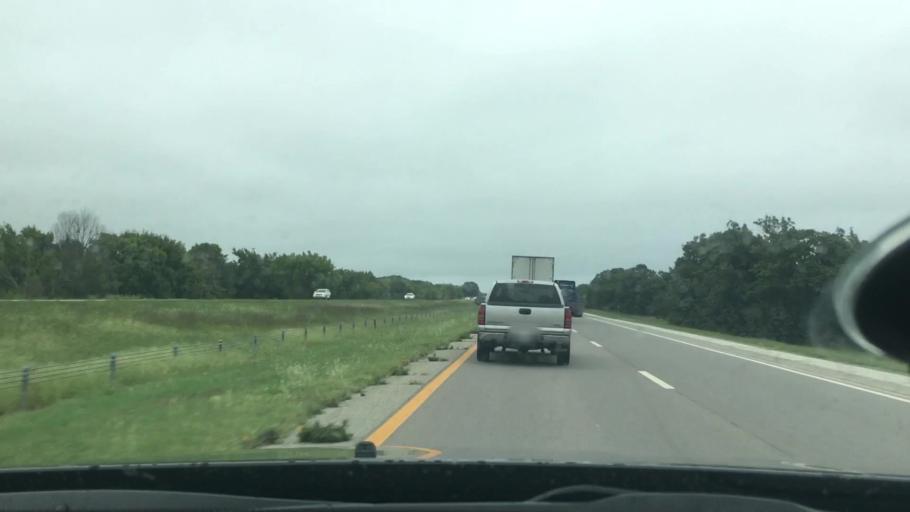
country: US
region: Oklahoma
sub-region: Okfuskee County
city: Okemah
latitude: 35.4283
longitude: -96.2389
